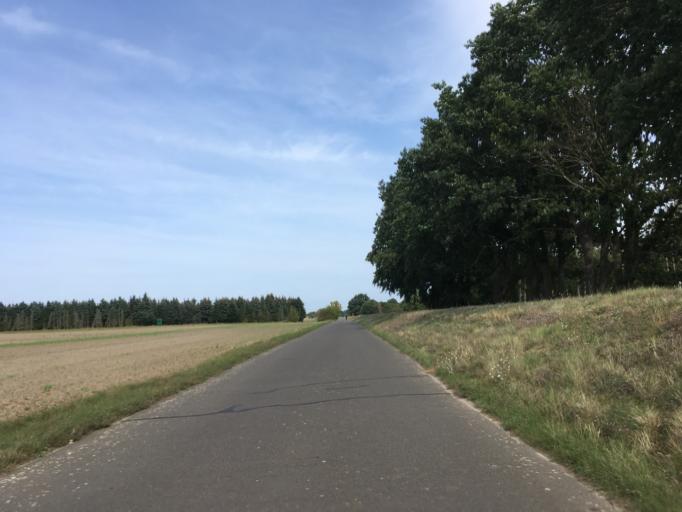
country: DE
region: Brandenburg
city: Guben
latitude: 51.9827
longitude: 14.7123
